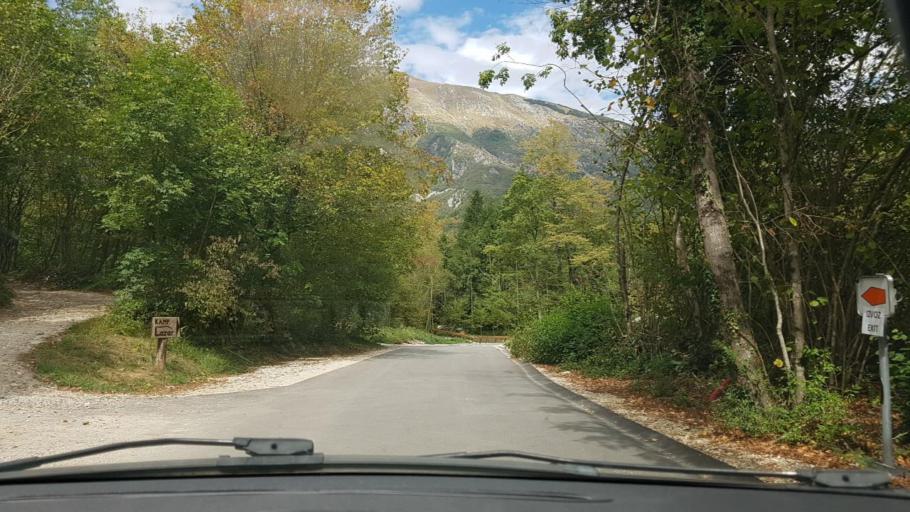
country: SI
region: Kobarid
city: Kobarid
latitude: 46.2538
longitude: 13.5850
